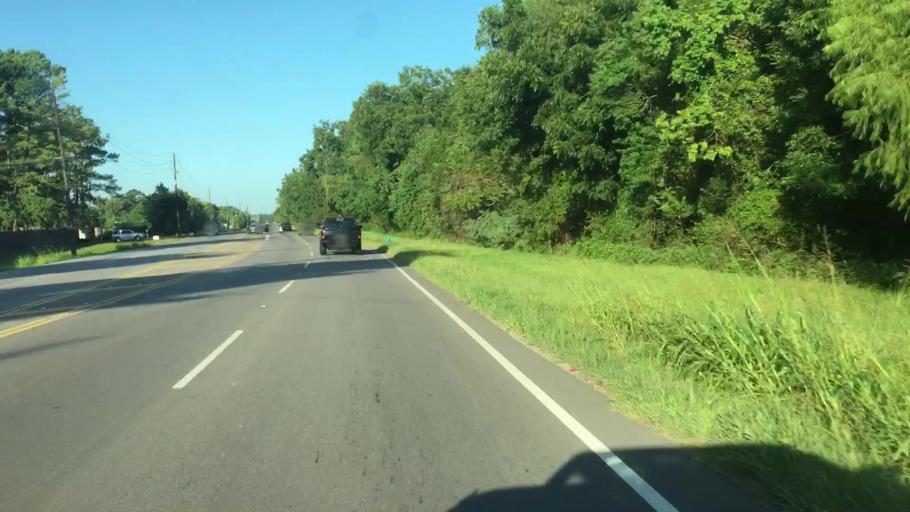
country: US
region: Texas
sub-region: Harris County
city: Humble
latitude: 29.9617
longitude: -95.2542
